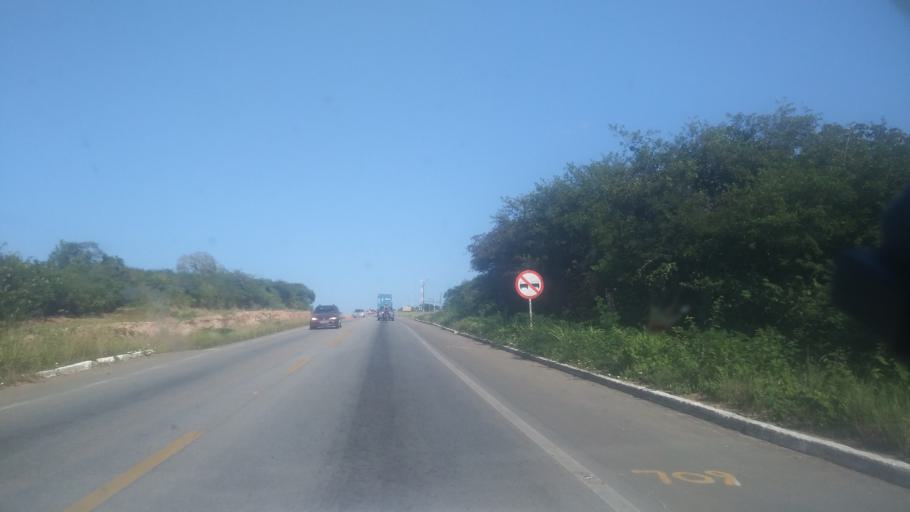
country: BR
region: Rio Grande do Norte
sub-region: Macaiba
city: Macaiba
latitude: -5.8669
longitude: -35.3647
